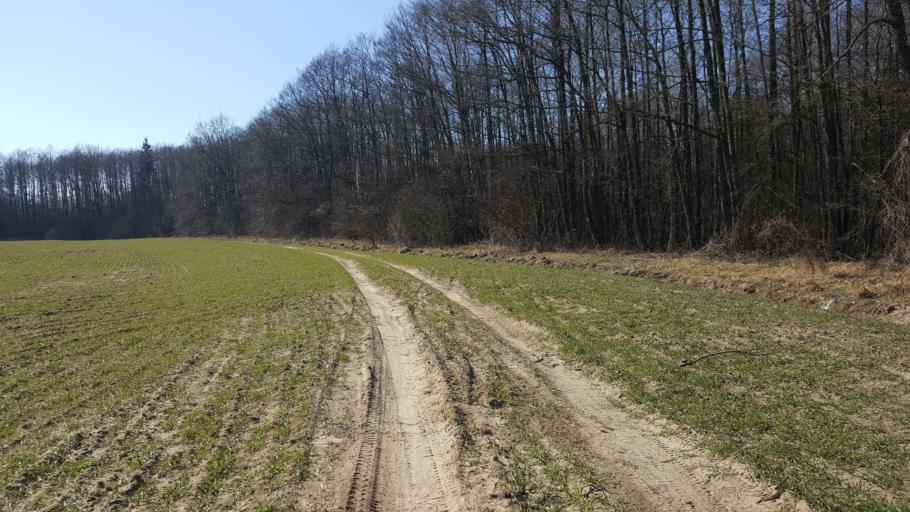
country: BY
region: Brest
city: Kamyanyets
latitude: 52.3663
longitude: 23.7662
